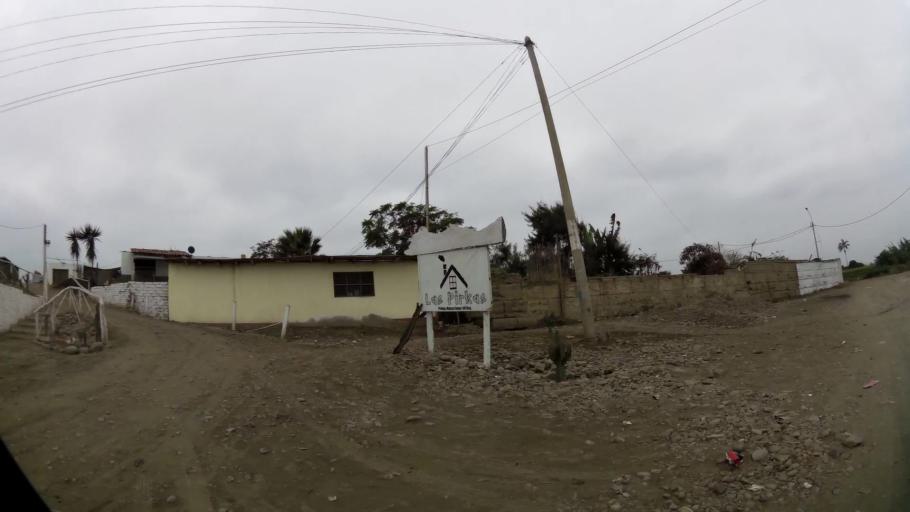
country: PE
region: Lima
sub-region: Barranca
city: Barranca
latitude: -10.7622
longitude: -77.7586
